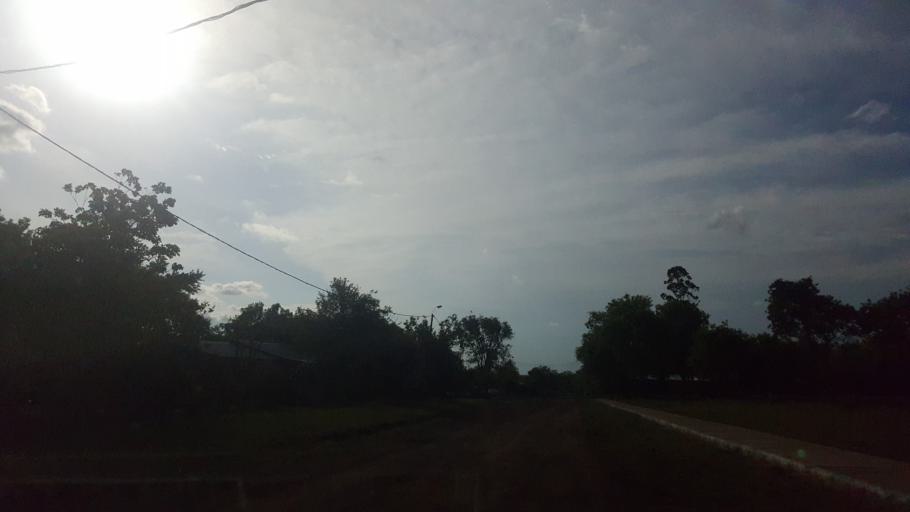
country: AR
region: Misiones
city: Cerro Cora
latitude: -27.5624
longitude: -55.7047
